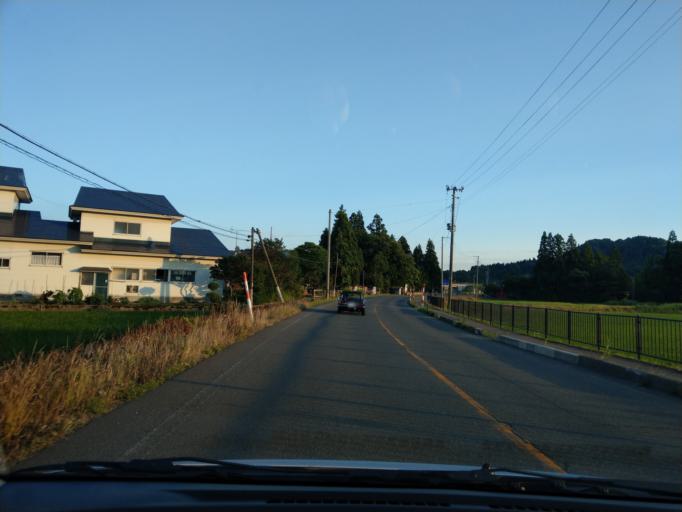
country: JP
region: Akita
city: Kakunodatemachi
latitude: 39.6147
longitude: 140.5712
